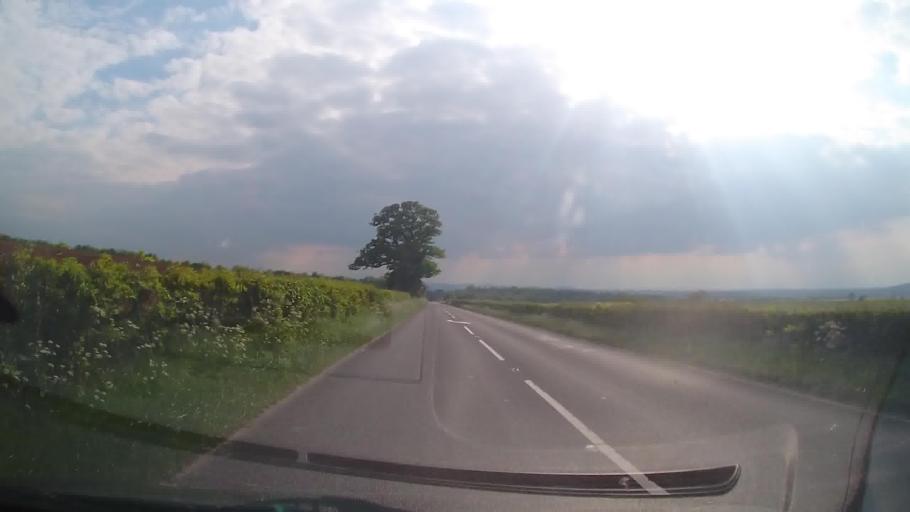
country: GB
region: England
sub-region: Shropshire
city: Withington
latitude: 52.6919
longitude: -2.5851
